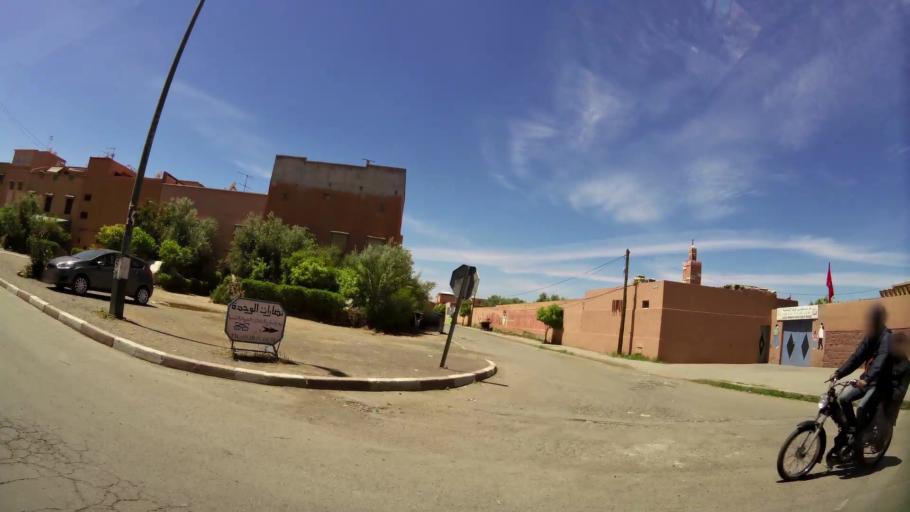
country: MA
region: Marrakech-Tensift-Al Haouz
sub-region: Marrakech
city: Marrakesh
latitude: 31.6323
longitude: -8.0453
